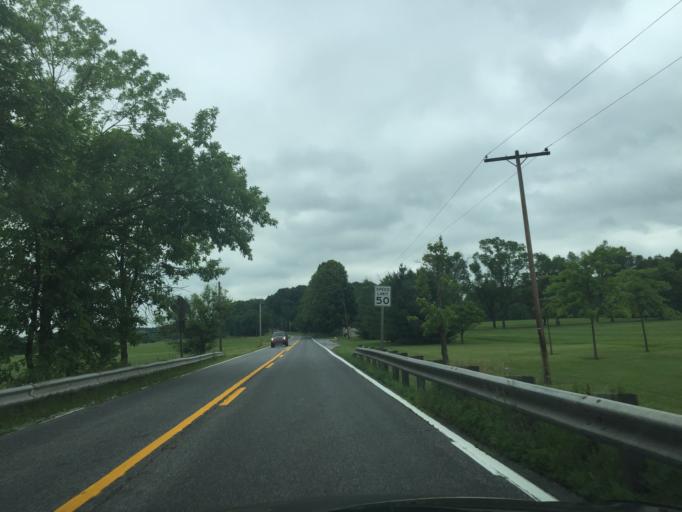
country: US
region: Maryland
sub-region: Harford County
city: Jarrettsville
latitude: 39.5448
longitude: -76.5303
